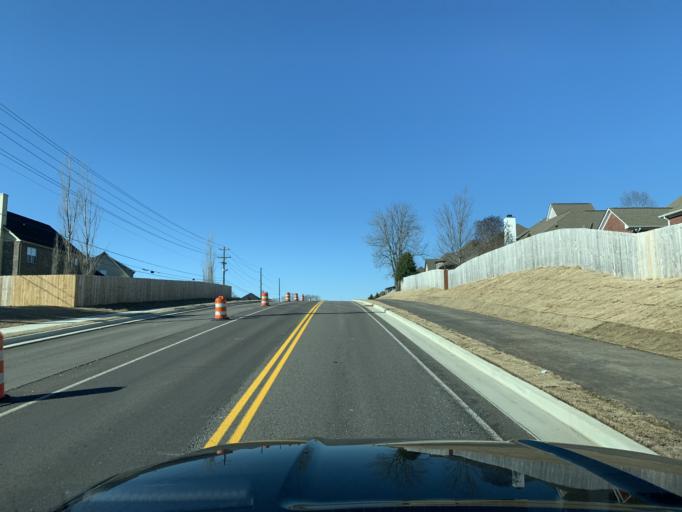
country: US
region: Tennessee
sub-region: Maury County
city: Spring Hill
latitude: 35.7528
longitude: -86.8780
